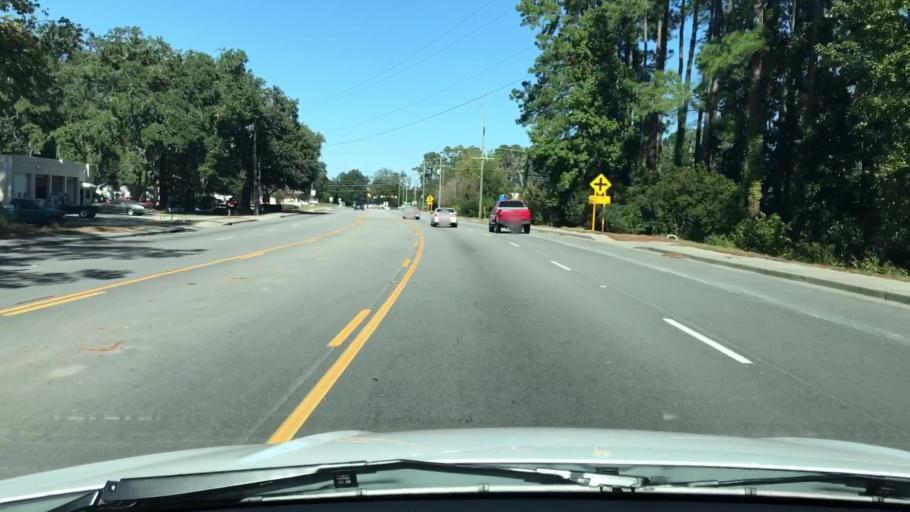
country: US
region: South Carolina
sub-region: Beaufort County
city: Burton
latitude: 32.4385
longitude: -80.7223
